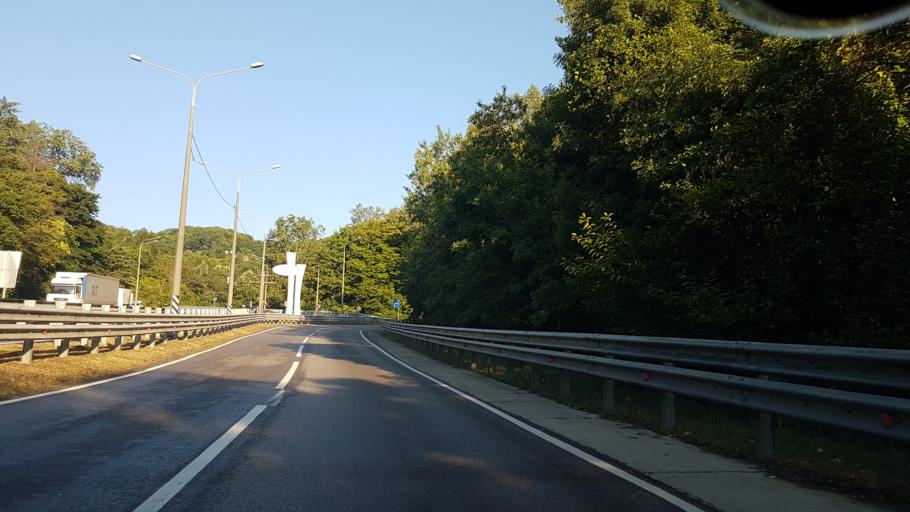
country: RU
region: Krasnodarskiy
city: Dagomys
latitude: 43.6445
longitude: 39.6974
